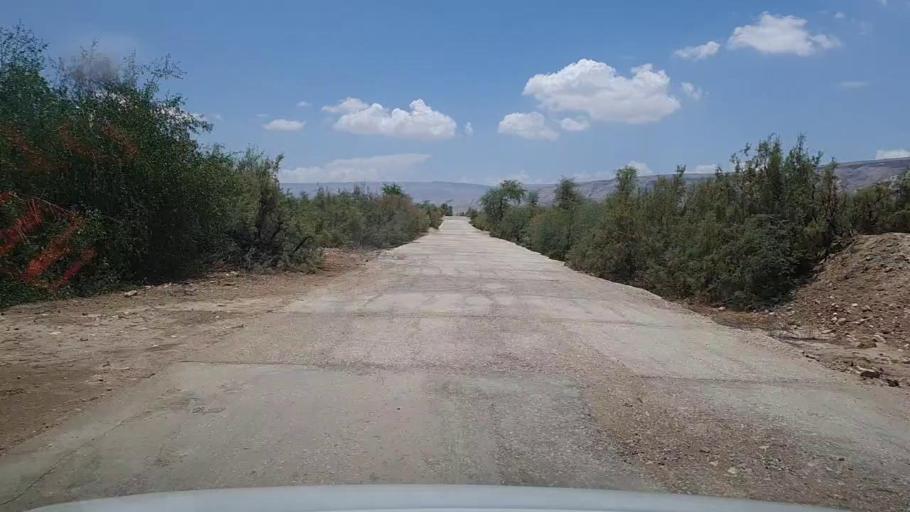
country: PK
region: Sindh
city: Bhan
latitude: 26.2774
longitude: 67.5272
